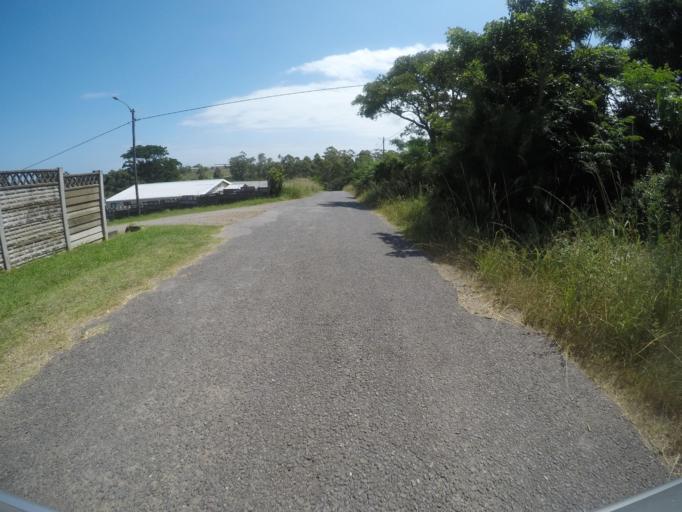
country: ZA
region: Eastern Cape
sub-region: Buffalo City Metropolitan Municipality
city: East London
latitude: -32.9687
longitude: 27.8556
